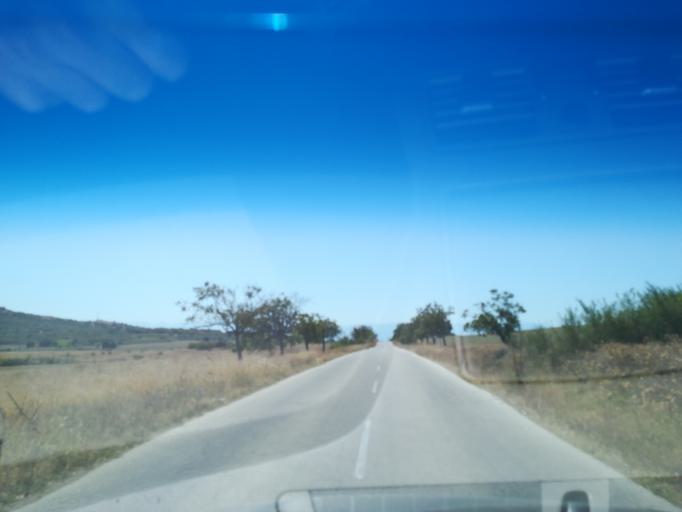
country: BG
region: Pazardzhik
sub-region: Obshtina Pazardzhik
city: Pazardzhik
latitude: 42.3181
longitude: 24.4069
